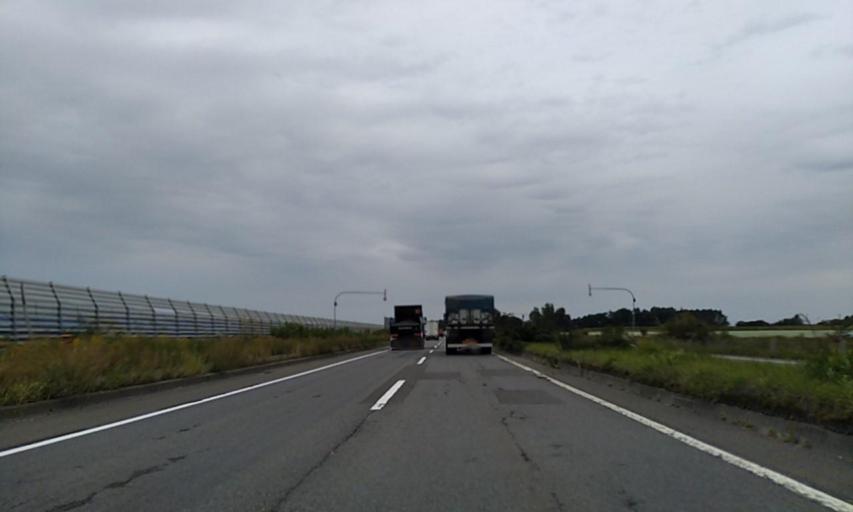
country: JP
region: Hokkaido
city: Ishikari
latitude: 43.1564
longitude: 141.2429
